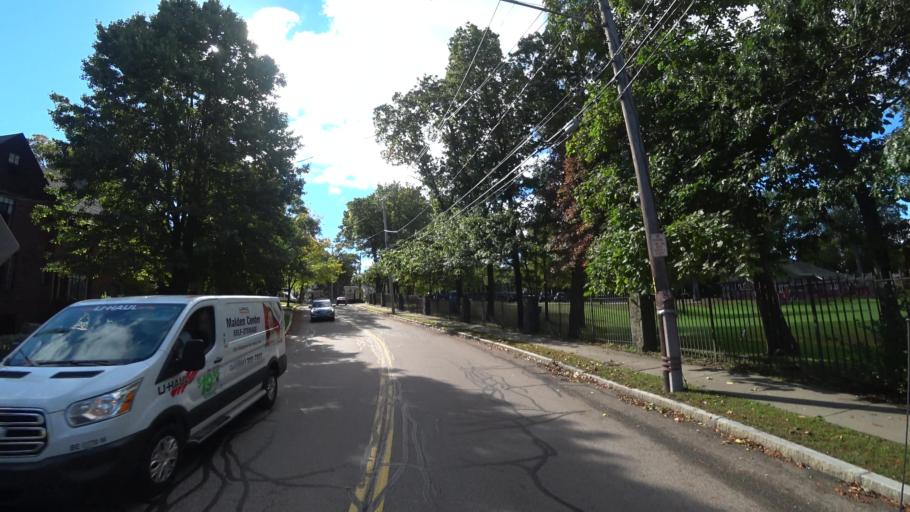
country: US
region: Massachusetts
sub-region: Middlesex County
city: Watertown
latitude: 42.3523
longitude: -71.1800
